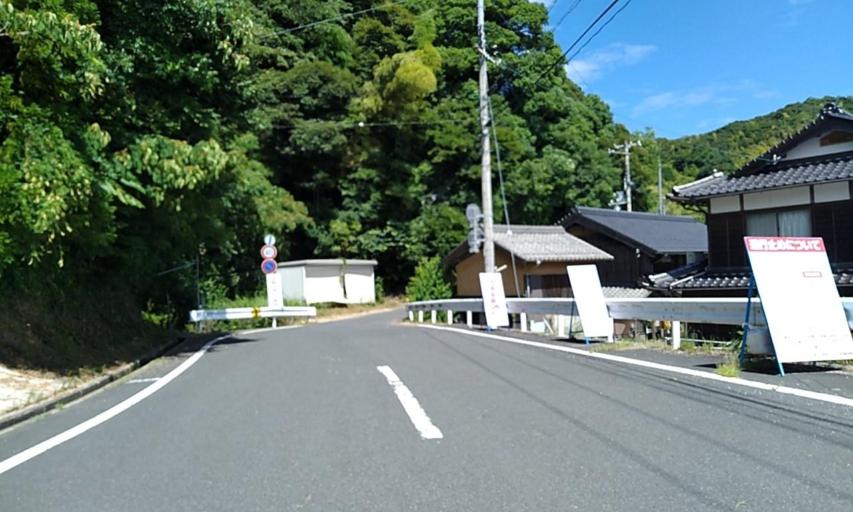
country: JP
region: Kyoto
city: Miyazu
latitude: 35.5736
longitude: 135.2498
